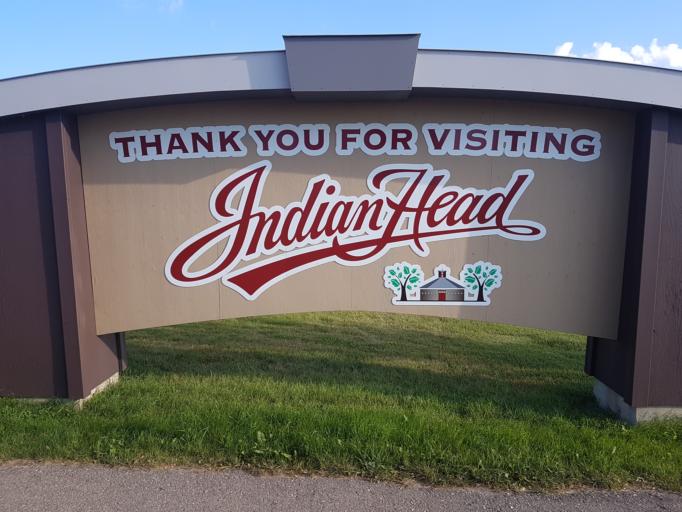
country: CA
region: Saskatchewan
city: Indian Head
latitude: 50.5270
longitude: -103.6781
